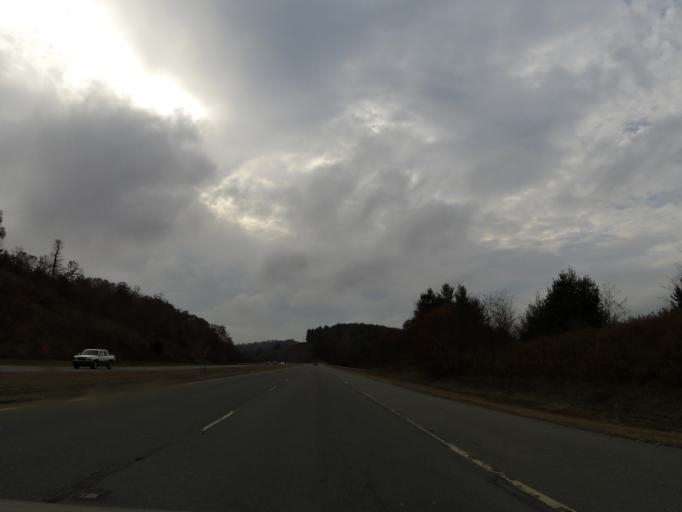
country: US
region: North Carolina
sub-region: Watauga County
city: Boone
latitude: 36.2350
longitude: -81.5675
